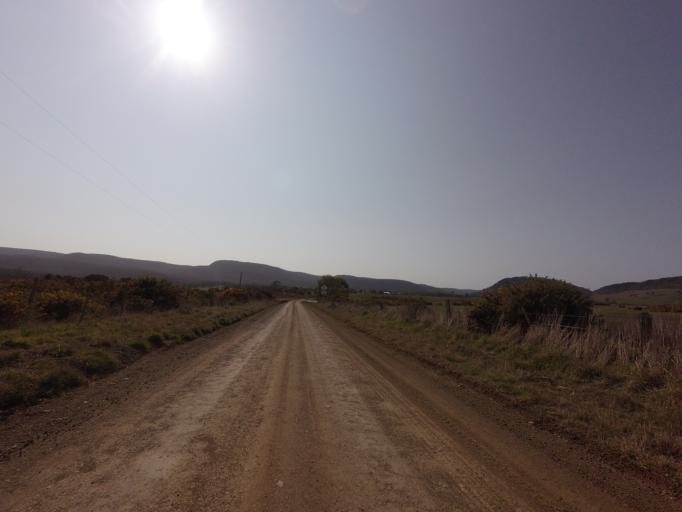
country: AU
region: Tasmania
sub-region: Break O'Day
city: St Helens
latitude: -41.8135
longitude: 147.9414
